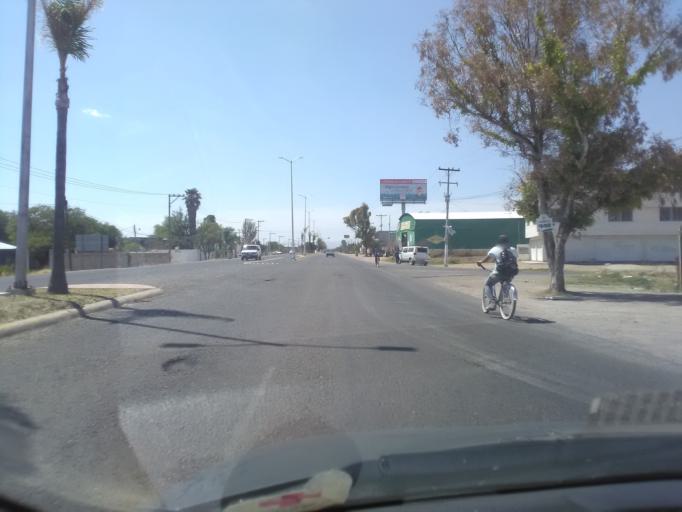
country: MX
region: Durango
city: Victoria de Durango
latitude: 24.0265
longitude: -104.5754
